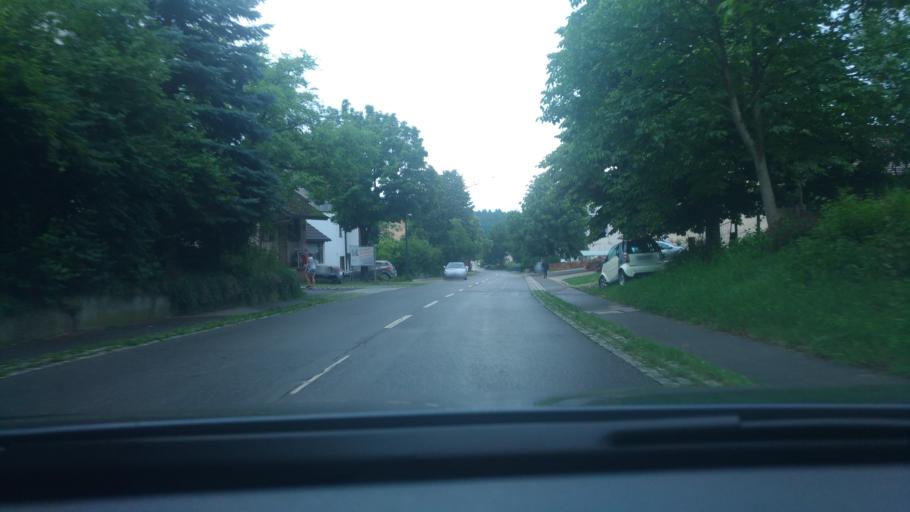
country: DE
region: Baden-Wuerttemberg
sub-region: Tuebingen Region
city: Sipplingen
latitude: 47.8313
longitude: 9.0956
